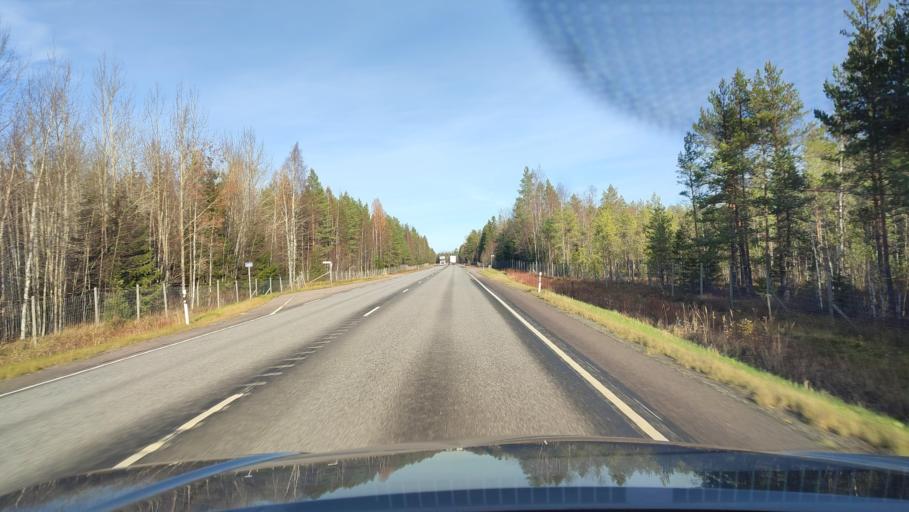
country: FI
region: Ostrobothnia
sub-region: Vaasa
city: Malax
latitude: 62.8297
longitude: 21.6925
